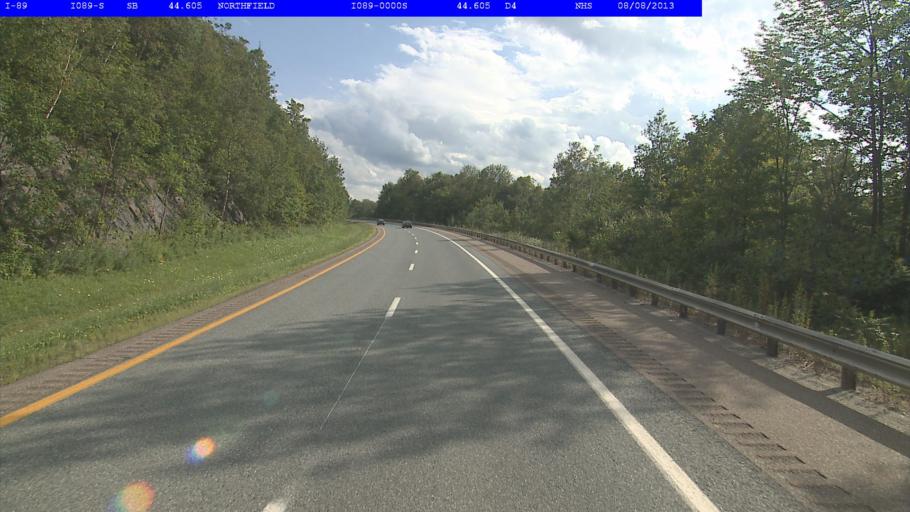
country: US
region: Vermont
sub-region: Washington County
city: Northfield
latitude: 44.1385
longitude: -72.6008
